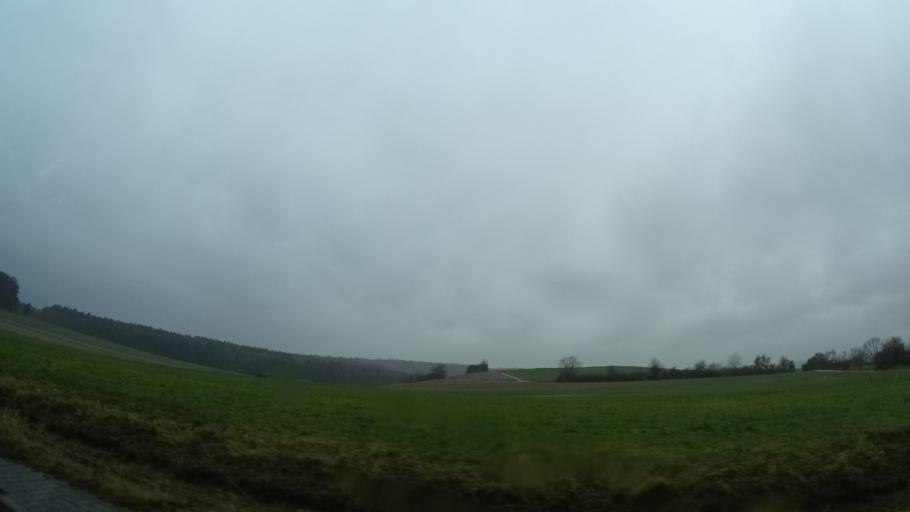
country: DE
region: Hesse
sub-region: Regierungsbezirk Kassel
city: Hofbieber
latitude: 50.5681
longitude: 9.8294
